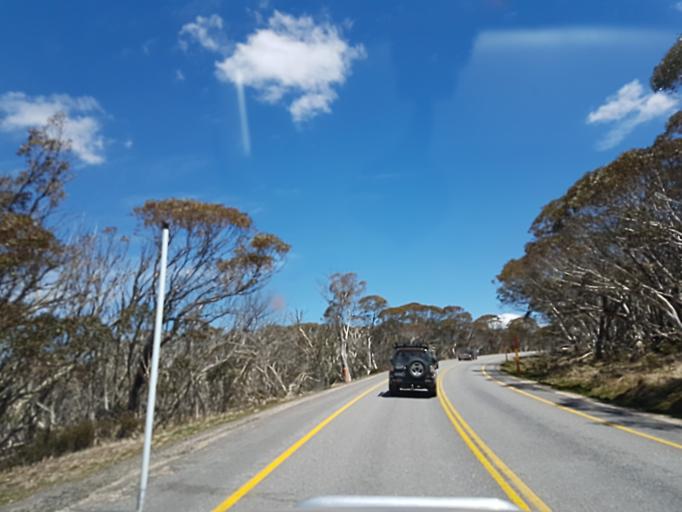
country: AU
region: Victoria
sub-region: Alpine
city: Mount Beauty
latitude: -37.0218
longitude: 147.2263
